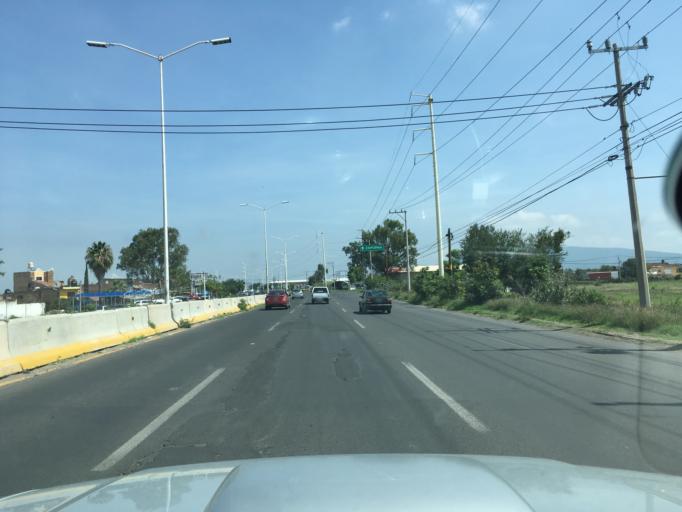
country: MX
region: Jalisco
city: Tonala
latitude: 20.6732
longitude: -103.2368
